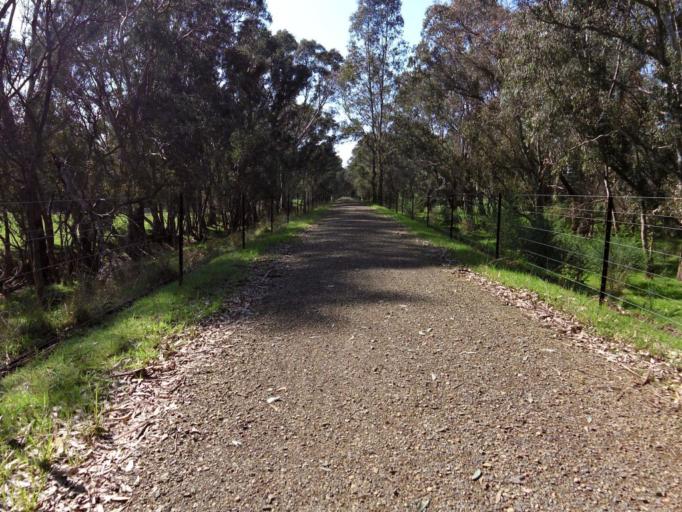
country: AU
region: Victoria
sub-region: Murrindindi
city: Alexandra
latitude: -37.1619
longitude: 145.5526
